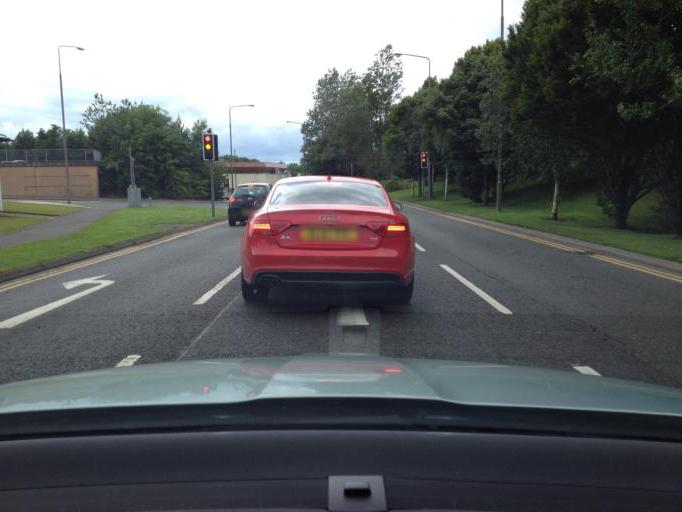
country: GB
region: Scotland
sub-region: West Lothian
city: Livingston
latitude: 55.8875
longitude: -3.5082
